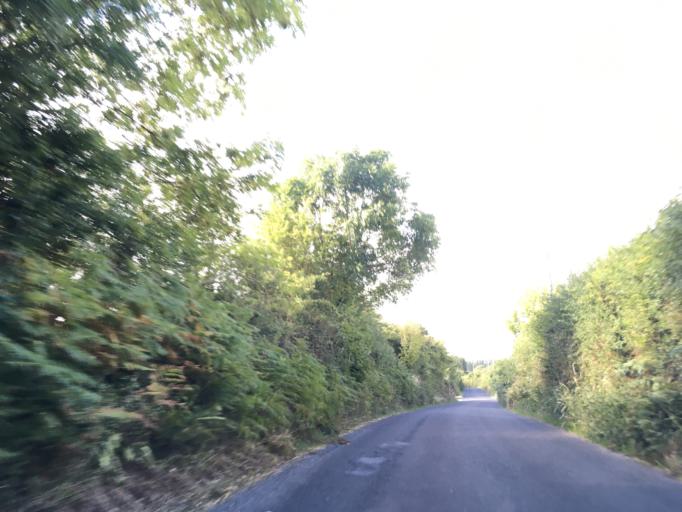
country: IE
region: Munster
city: Cahir
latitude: 52.2717
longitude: -7.9562
